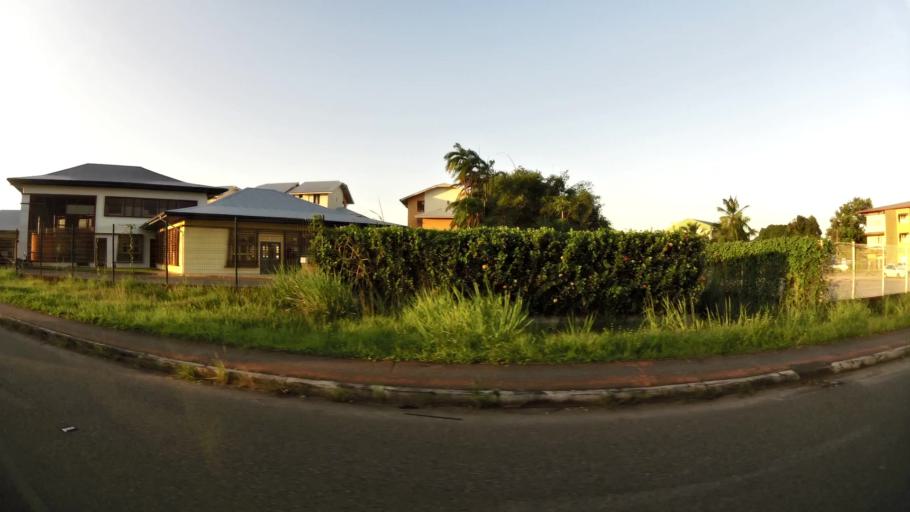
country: GF
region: Guyane
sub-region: Guyane
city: Cayenne
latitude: 4.9328
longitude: -52.3086
